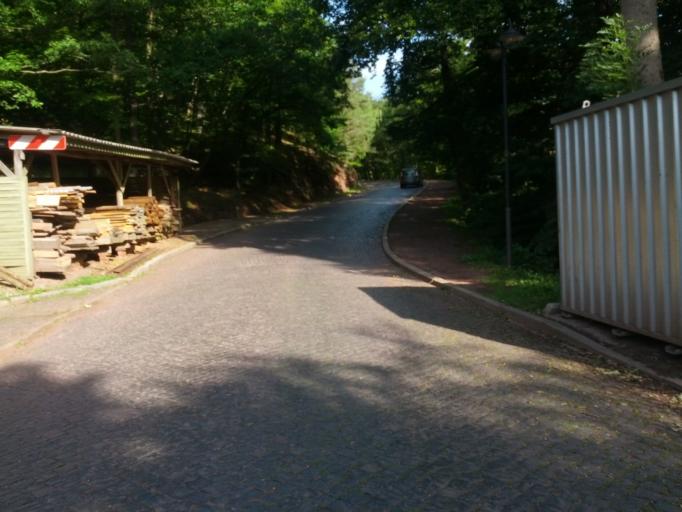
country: DE
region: Thuringia
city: Eisenach
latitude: 50.9671
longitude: 10.3013
